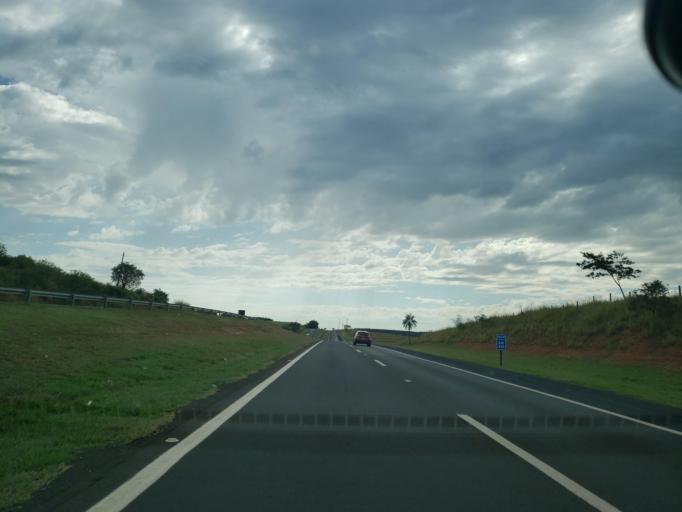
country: BR
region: Sao Paulo
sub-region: Cafelandia
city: Cafelandia
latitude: -21.7805
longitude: -49.6586
